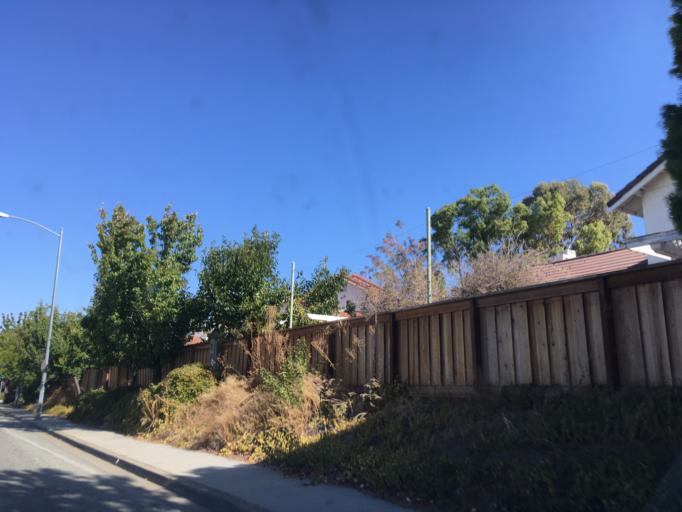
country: US
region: California
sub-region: Santa Clara County
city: Milpitas
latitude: 37.4229
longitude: -121.8692
